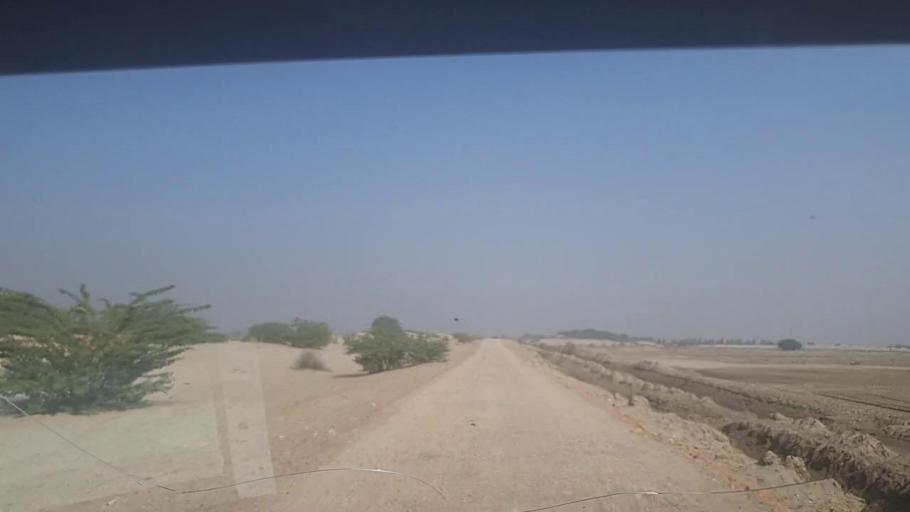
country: PK
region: Sindh
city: Khairpur
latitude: 27.4487
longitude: 68.7196
